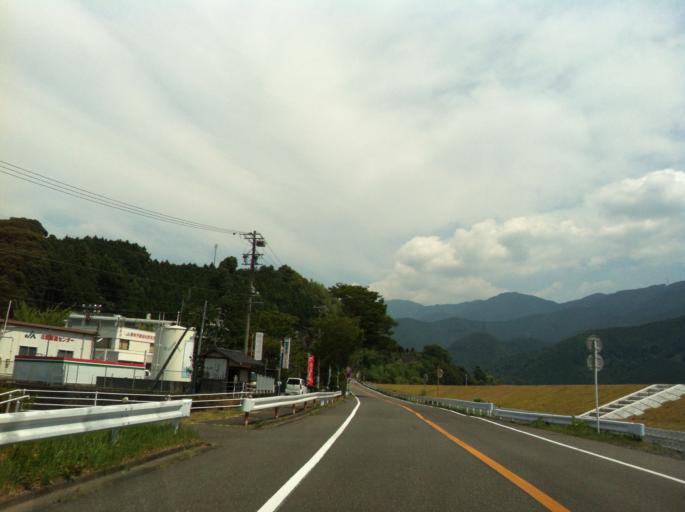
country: JP
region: Shizuoka
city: Shizuoka-shi
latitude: 35.0749
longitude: 138.3673
